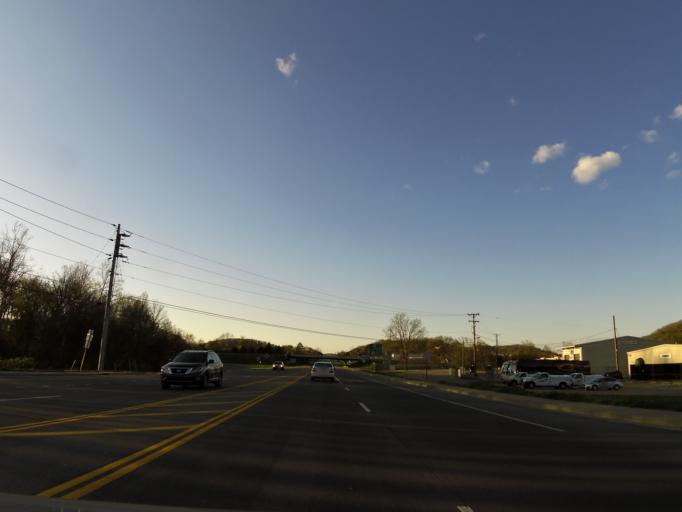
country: US
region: Tennessee
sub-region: Davidson County
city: Goodlettsville
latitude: 36.3401
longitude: -86.7183
